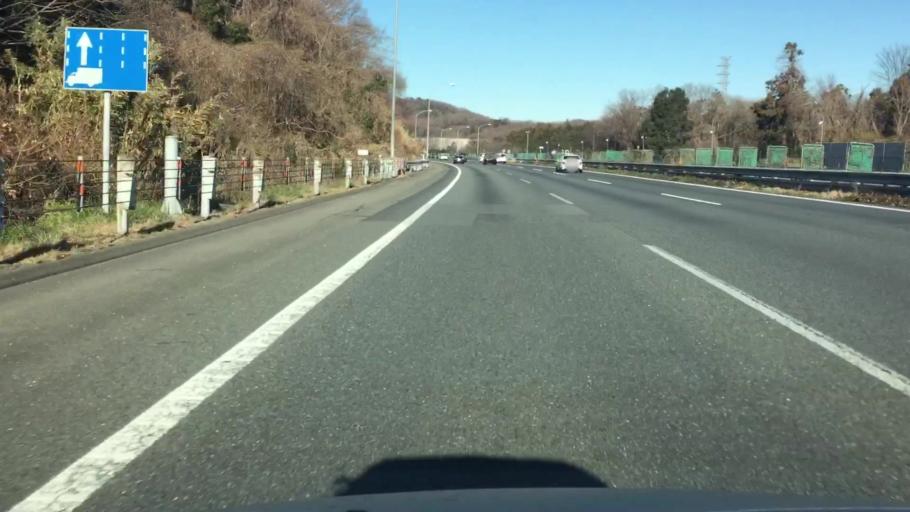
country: JP
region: Saitama
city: Ogawa
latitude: 36.0796
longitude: 139.2992
